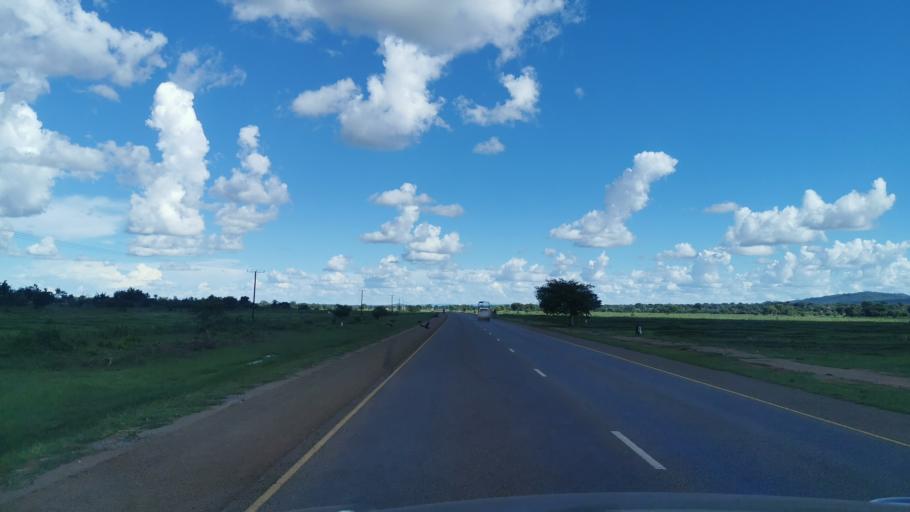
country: TZ
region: Geita
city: Ushirombo
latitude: -3.4776
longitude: 31.9161
